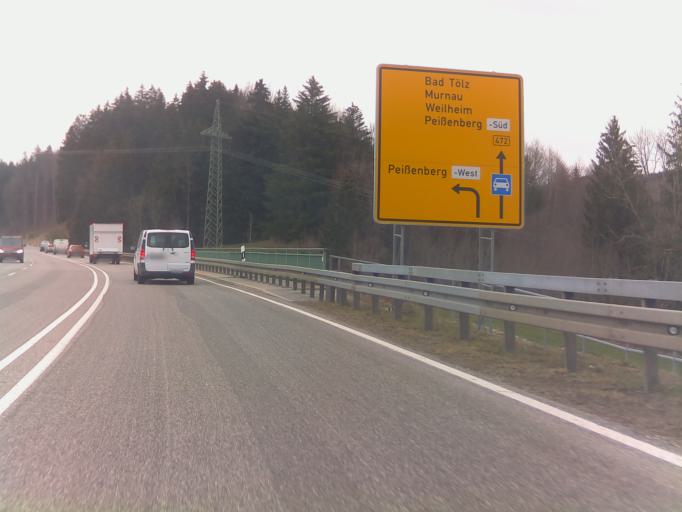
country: DE
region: Bavaria
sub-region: Upper Bavaria
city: Peissenberg
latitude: 47.7807
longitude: 11.0374
